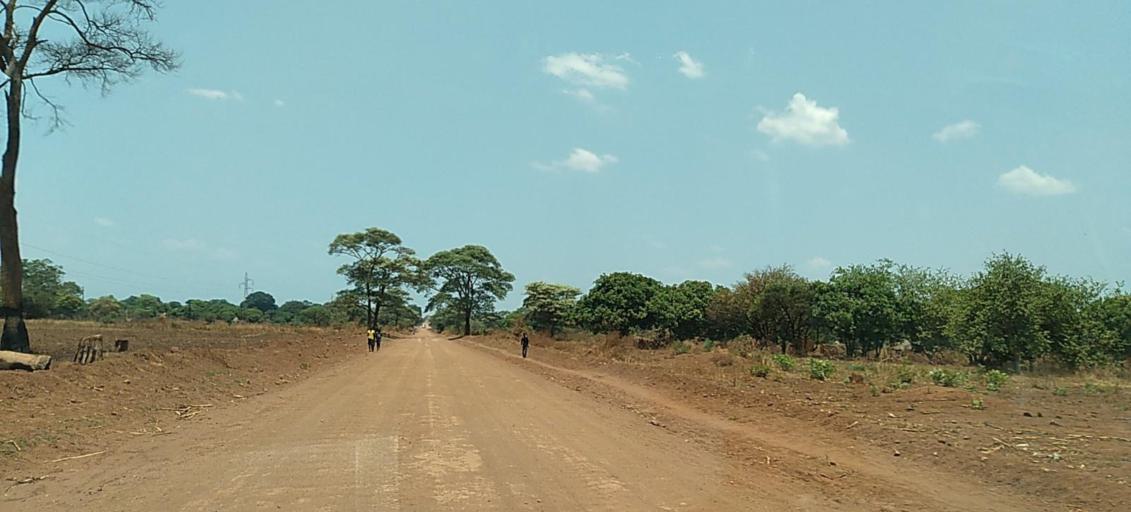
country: ZM
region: Copperbelt
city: Mpongwe
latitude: -13.5142
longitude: 28.0276
